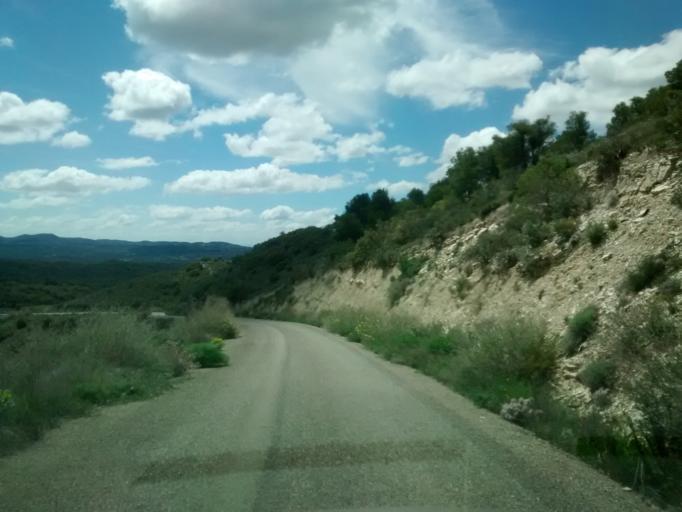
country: ES
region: Aragon
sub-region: Provincia de Huesca
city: Alcubierre
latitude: 41.8275
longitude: -0.5180
